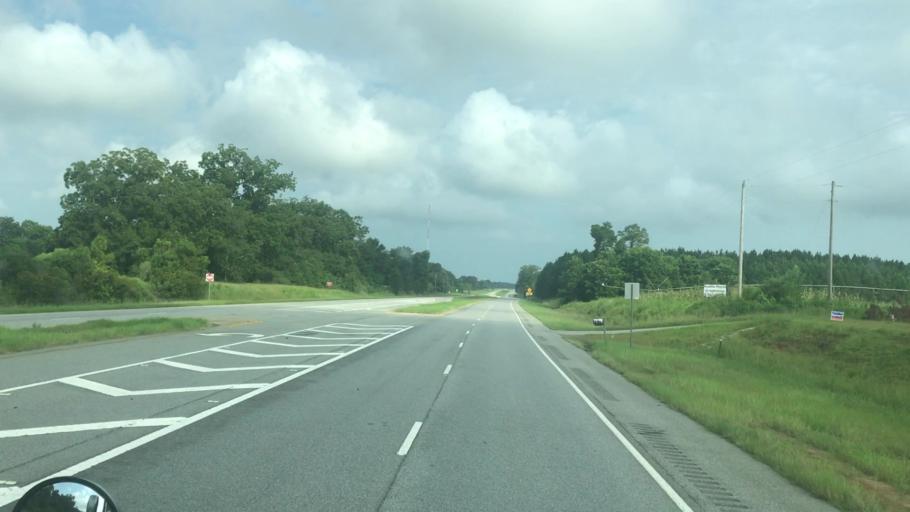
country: US
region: Georgia
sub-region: Miller County
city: Colquitt
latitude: 31.2564
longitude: -84.8066
